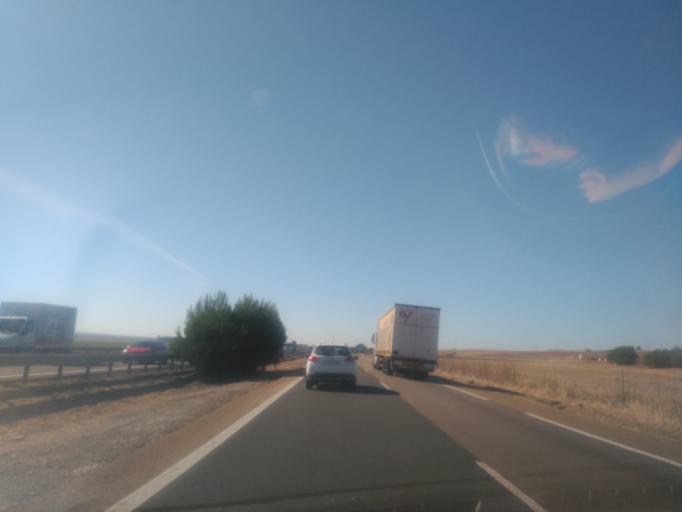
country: ES
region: Castille and Leon
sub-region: Provincia de Valladolid
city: Geria
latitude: 41.5530
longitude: -4.8785
